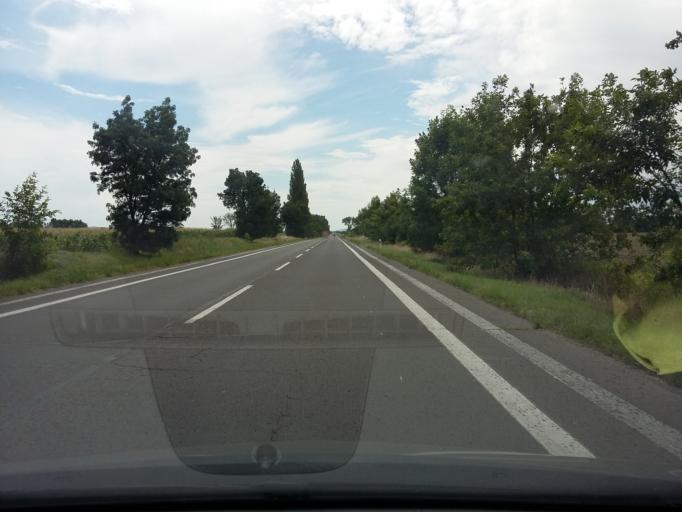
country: SK
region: Bratislavsky
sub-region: Okres Malacky
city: Malacky
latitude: 48.4624
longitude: 17.0109
